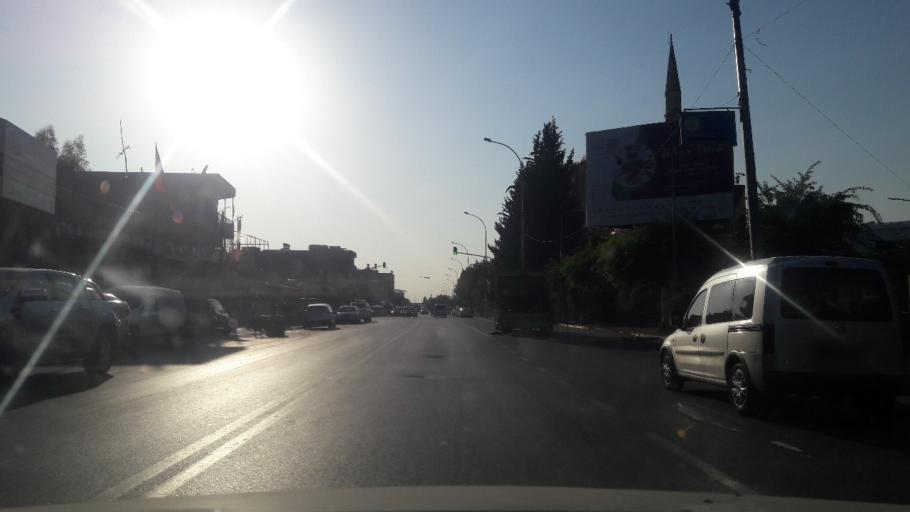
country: TR
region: Adana
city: Seyhan
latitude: 36.9874
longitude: 35.3041
